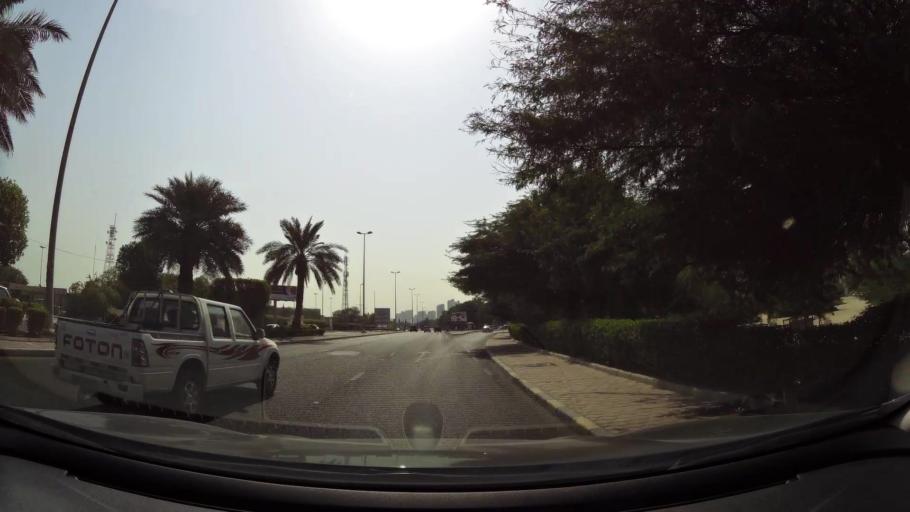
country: KW
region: Al Ahmadi
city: Al Fintas
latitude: 29.1716
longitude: 48.1228
